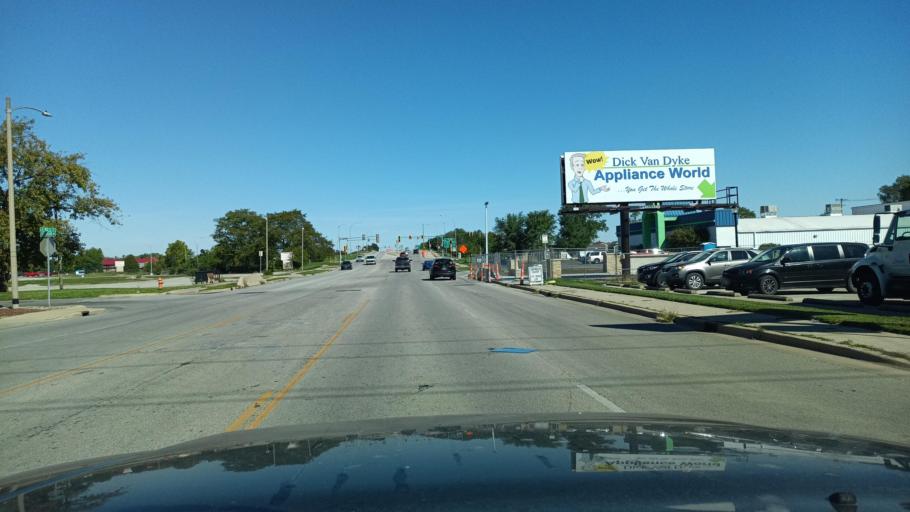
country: US
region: Illinois
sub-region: Champaign County
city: Champaign
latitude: 40.1308
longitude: -88.2436
